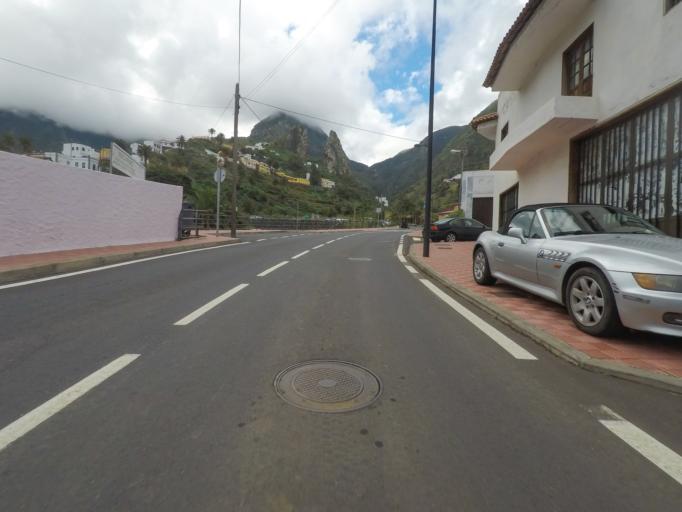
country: ES
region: Canary Islands
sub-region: Provincia de Santa Cruz de Tenerife
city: Hermigua
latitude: 28.1541
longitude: -17.1984
